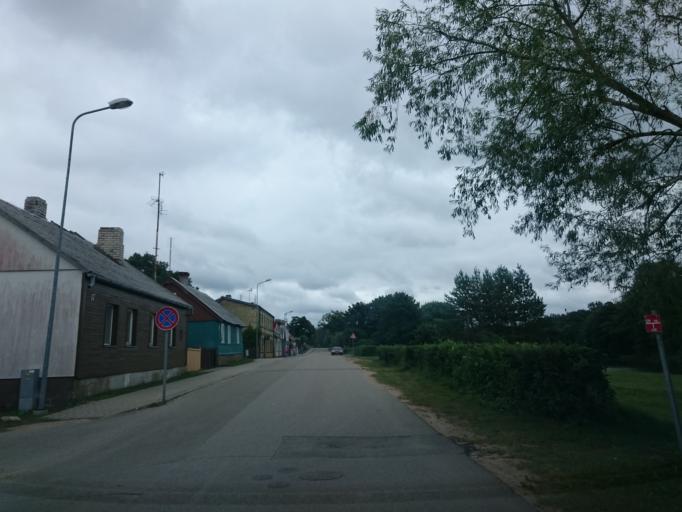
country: LV
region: Pavilostas
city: Pavilosta
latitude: 56.8886
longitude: 21.1765
